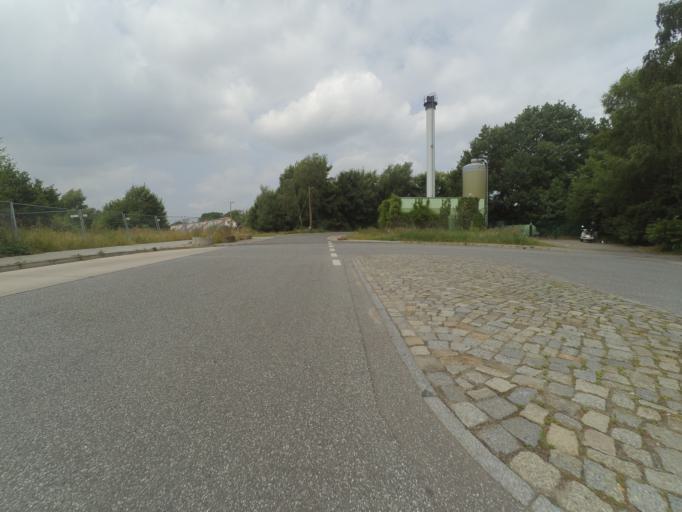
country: DE
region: Hamburg
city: Wandsbek
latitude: 53.5651
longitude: 10.1329
